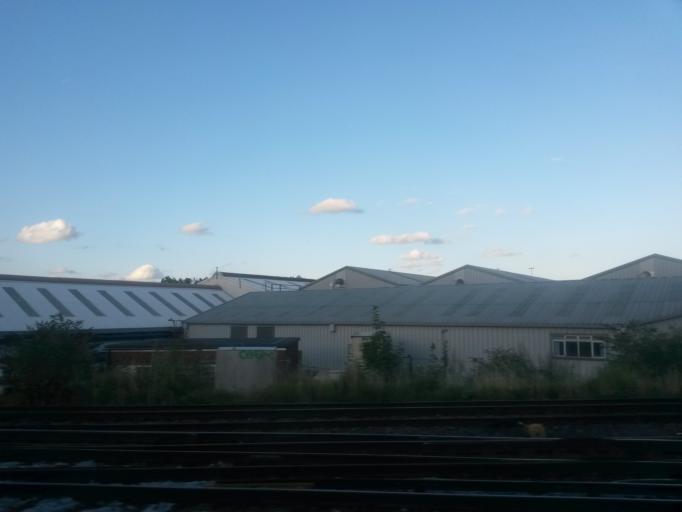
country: GB
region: England
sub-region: Greater London
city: Thornton Heath
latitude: 51.3910
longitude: -0.0878
